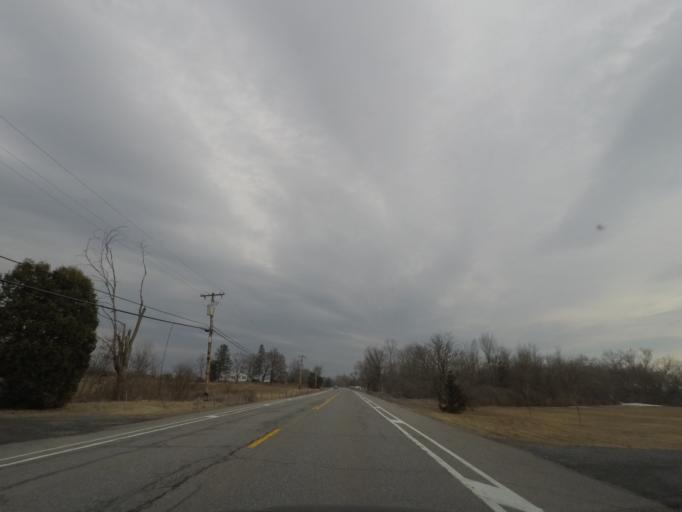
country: US
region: New York
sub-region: Washington County
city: Fort Edward
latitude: 43.2376
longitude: -73.5914
